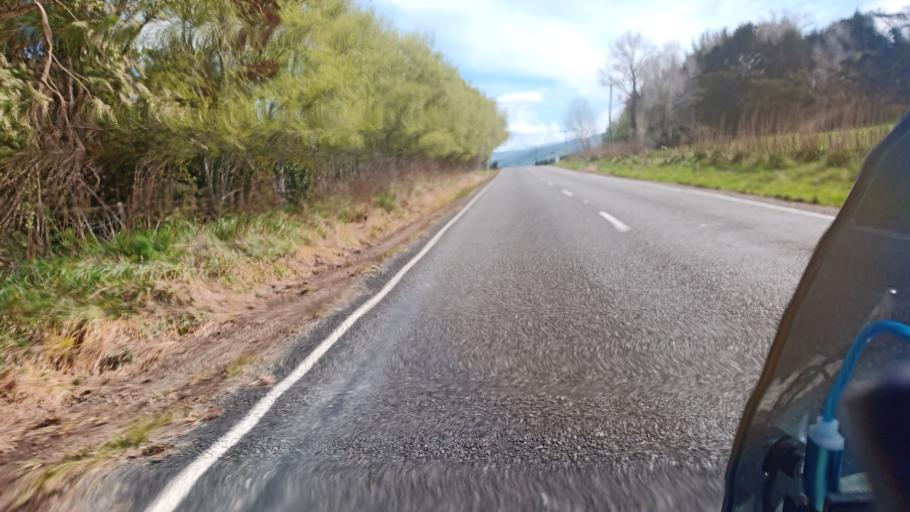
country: NZ
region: Gisborne
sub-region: Gisborne District
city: Gisborne
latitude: -37.8802
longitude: 178.2959
